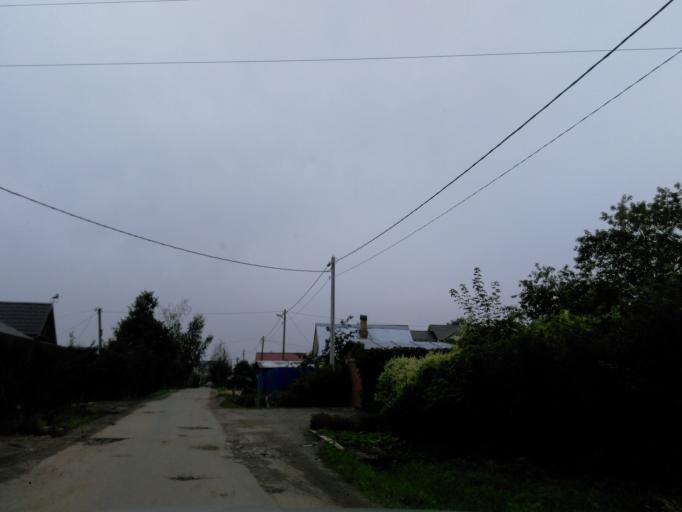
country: RU
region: Moskovskaya
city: Lozhki
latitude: 56.0681
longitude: 37.1194
